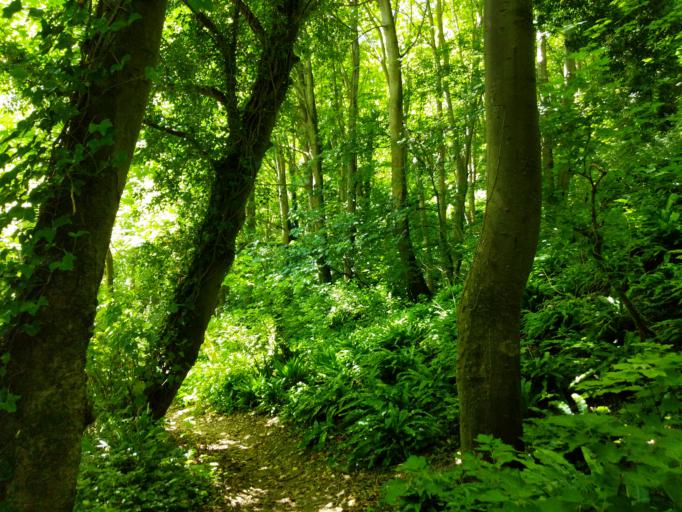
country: GB
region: England
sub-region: Kent
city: Folkestone
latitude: 51.1001
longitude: 1.2196
